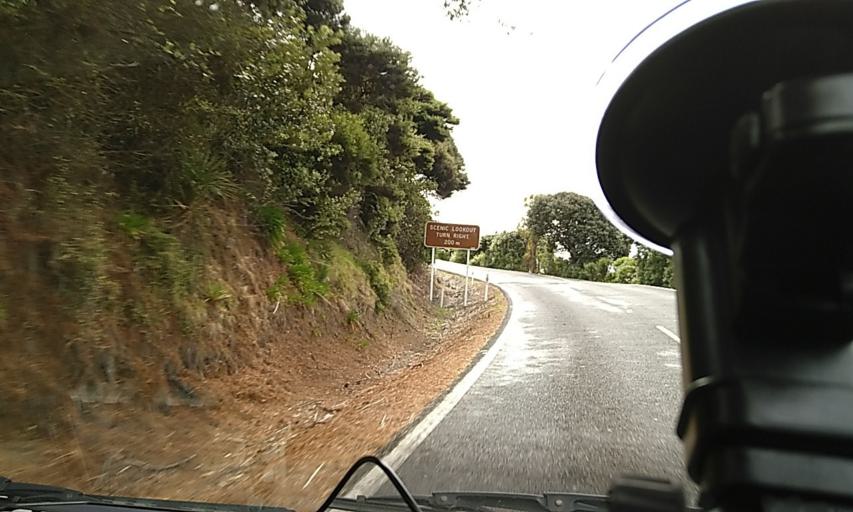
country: NZ
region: Northland
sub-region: Far North District
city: Ahipara
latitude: -35.5370
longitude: 173.3846
